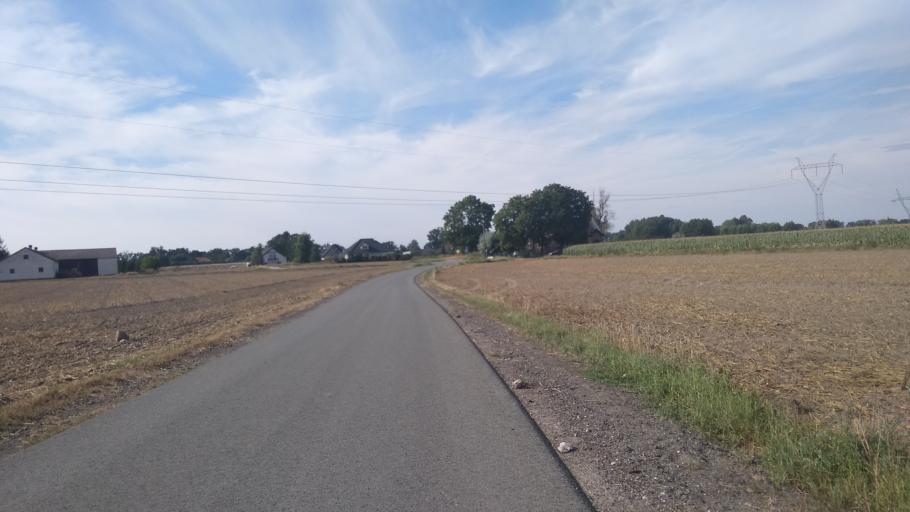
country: PL
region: Kujawsko-Pomorskie
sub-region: Powiat bydgoski
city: Osielsko
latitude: 53.2224
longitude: 18.1440
